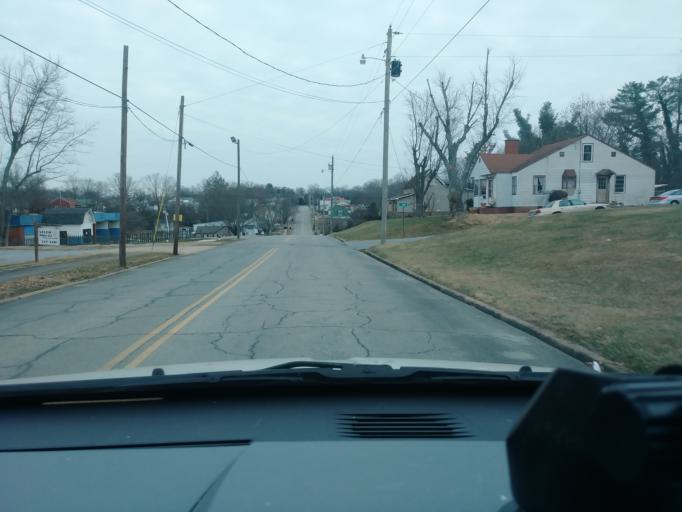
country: US
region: Tennessee
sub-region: Greene County
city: Greeneville
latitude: 36.1549
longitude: -82.8452
